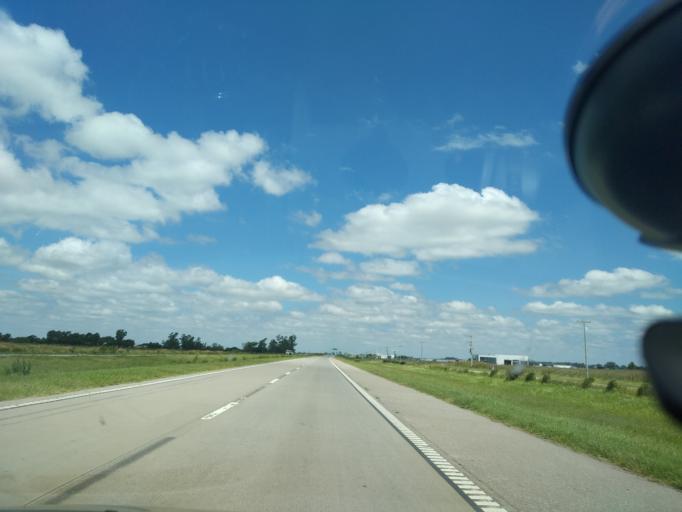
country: AR
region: Cordoba
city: Villa Maria
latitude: -32.3745
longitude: -63.2175
